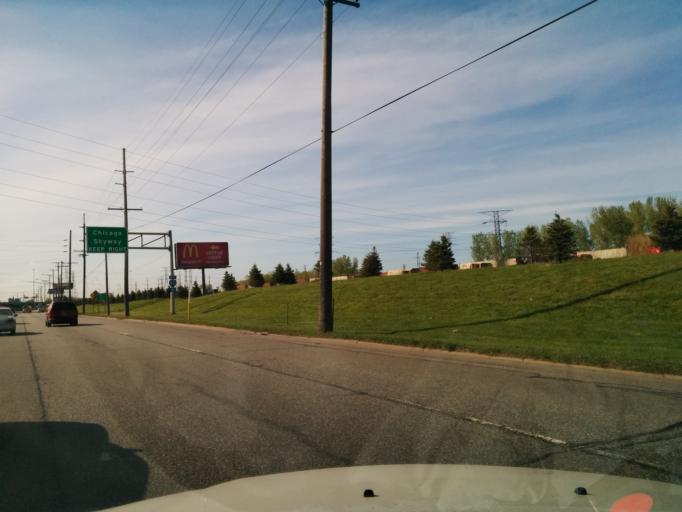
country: US
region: Indiana
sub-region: Lake County
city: Whiting
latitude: 41.6970
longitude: -87.5181
